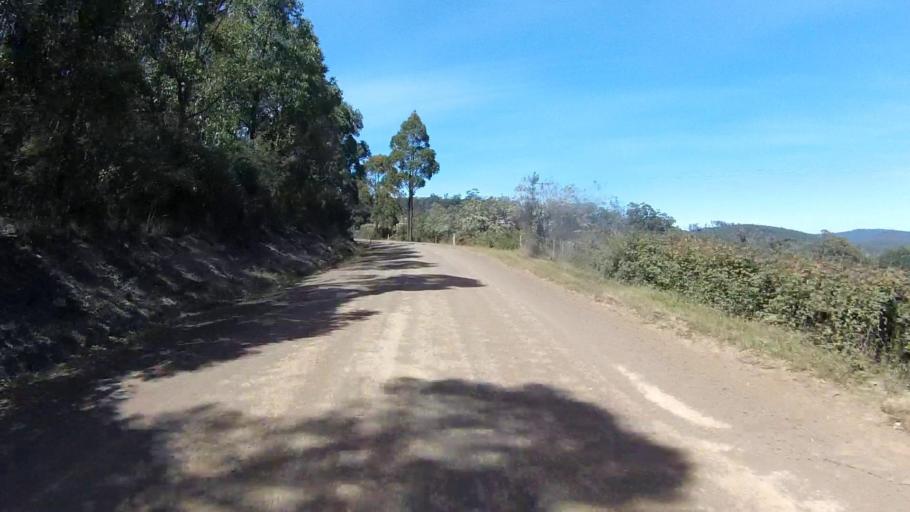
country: AU
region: Tasmania
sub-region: Sorell
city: Sorell
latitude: -42.6978
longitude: 147.7407
